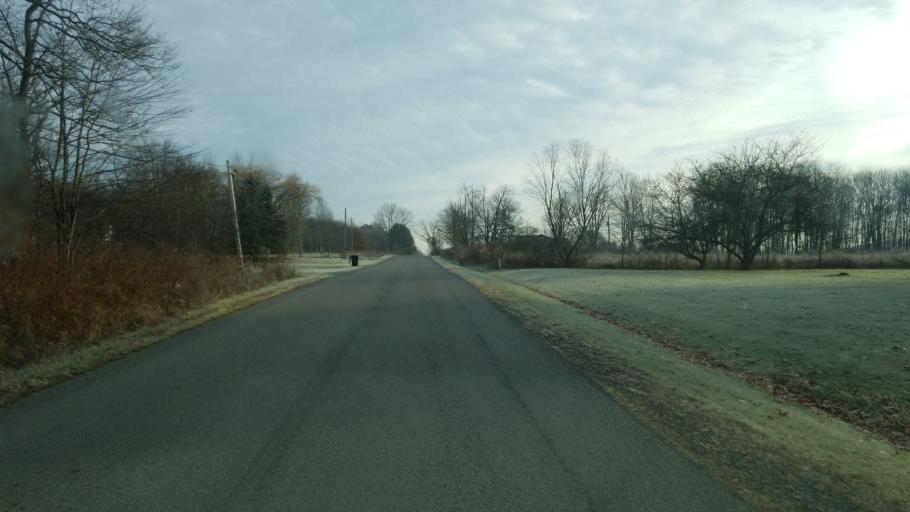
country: US
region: Pennsylvania
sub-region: Crawford County
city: Cochranton
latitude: 41.5098
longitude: -80.0812
